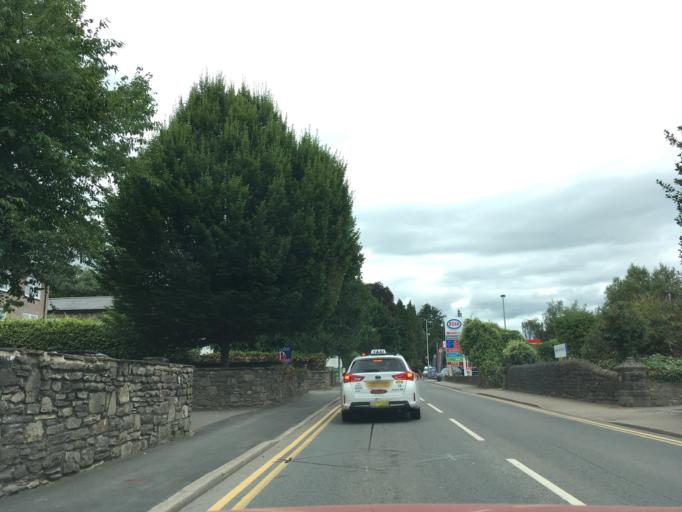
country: GB
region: Wales
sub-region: Monmouthshire
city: Abergavenny
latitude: 51.8230
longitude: -3.0152
